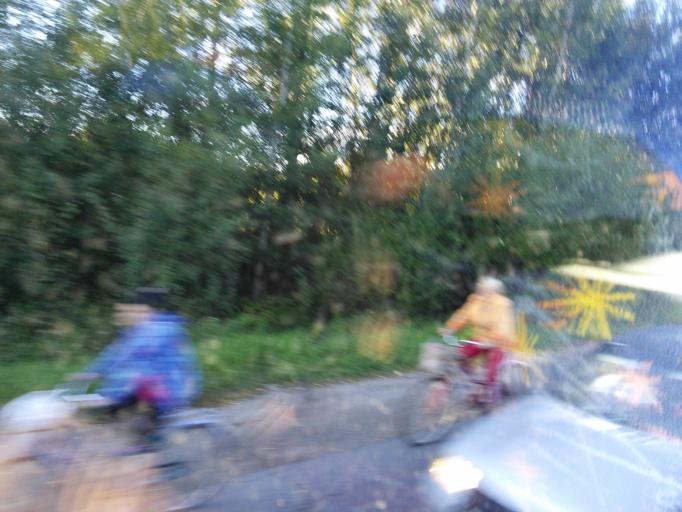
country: RU
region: Jaroslavl
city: Poshekhon'ye
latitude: 58.4957
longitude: 39.0967
